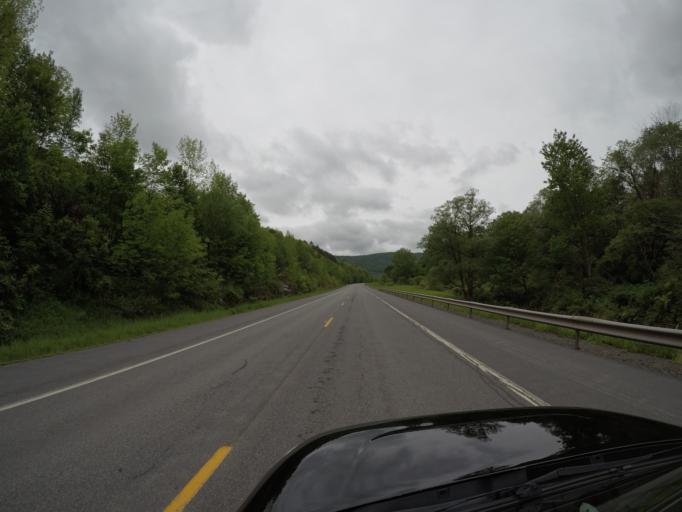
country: US
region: New York
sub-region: Delaware County
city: Stamford
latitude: 42.1325
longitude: -74.6624
